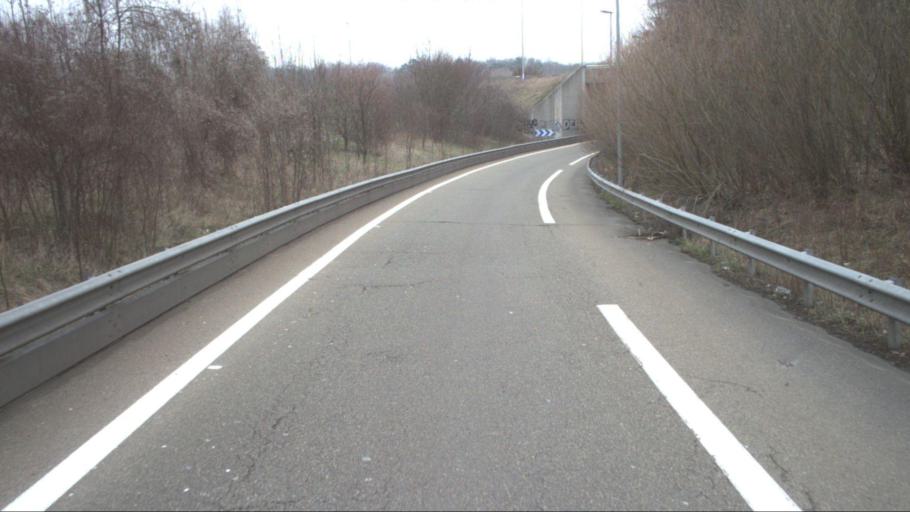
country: FR
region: Ile-de-France
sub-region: Departement des Yvelines
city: Villennes-sur-Seine
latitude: 48.9175
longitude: 2.0063
